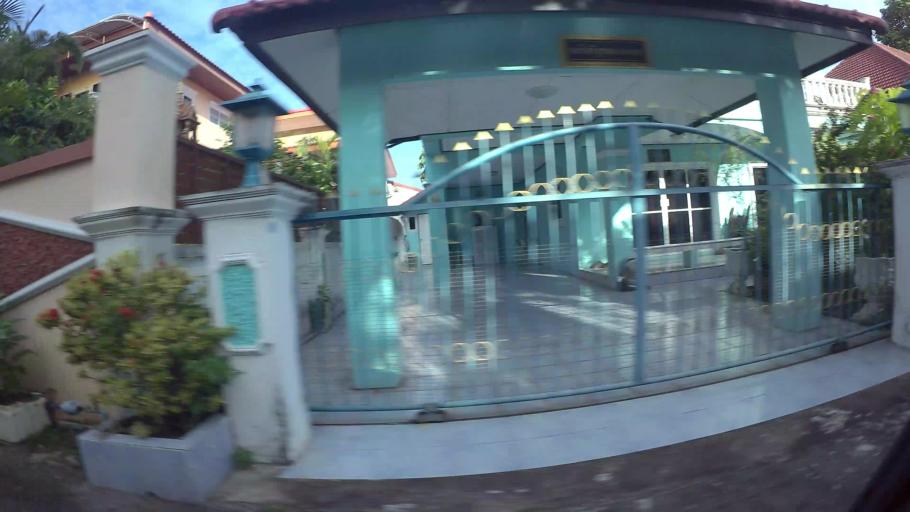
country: TH
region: Chon Buri
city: Sattahip
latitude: 12.6686
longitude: 100.9230
